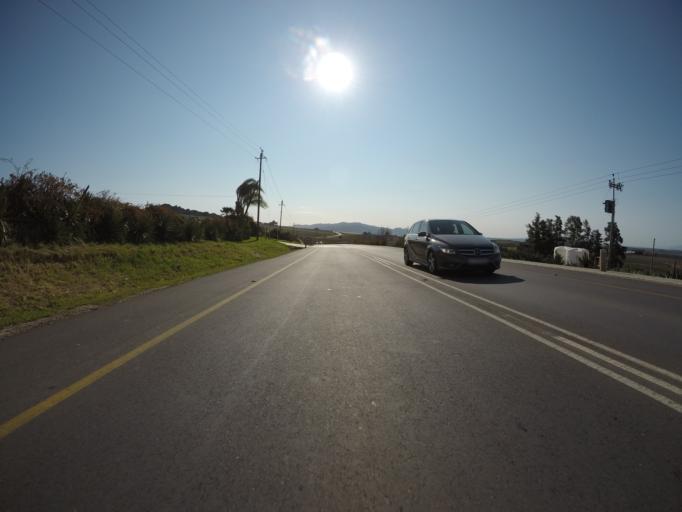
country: ZA
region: Western Cape
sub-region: Cape Winelands District Municipality
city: Noorder-Paarl
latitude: -33.6787
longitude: 18.9438
